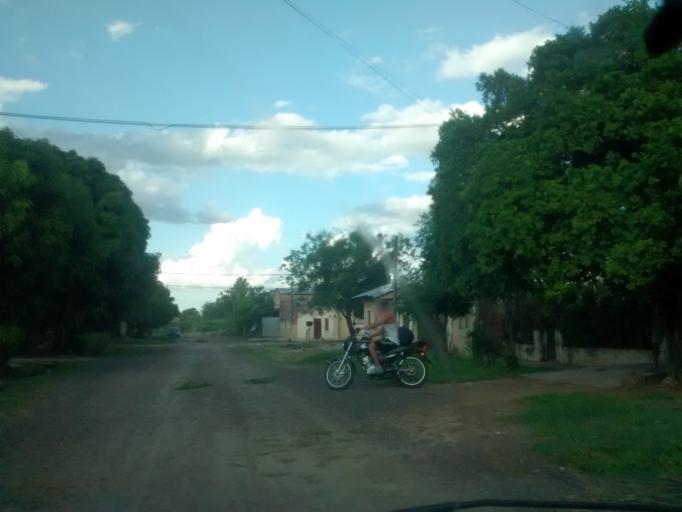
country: AR
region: Chaco
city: Fontana
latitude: -27.4388
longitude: -59.0118
